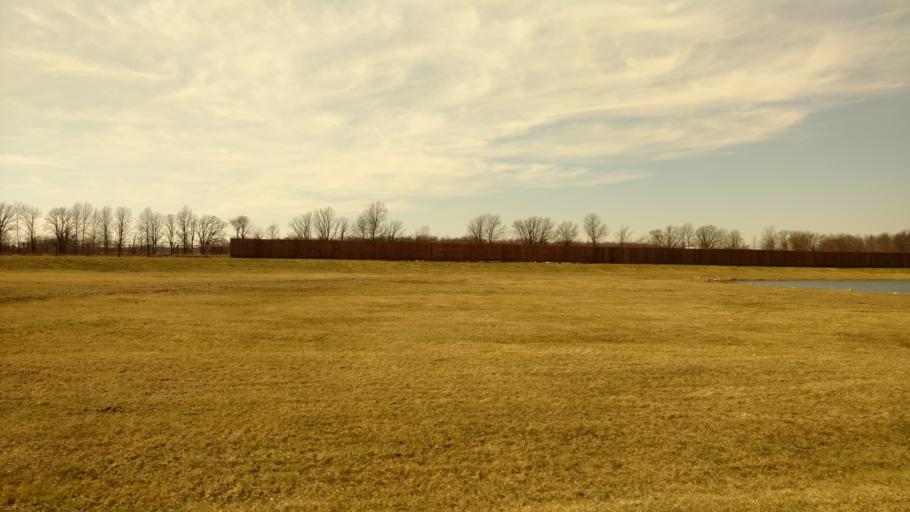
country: US
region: Ohio
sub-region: Hardin County
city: Kenton
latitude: 40.6062
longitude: -83.5034
